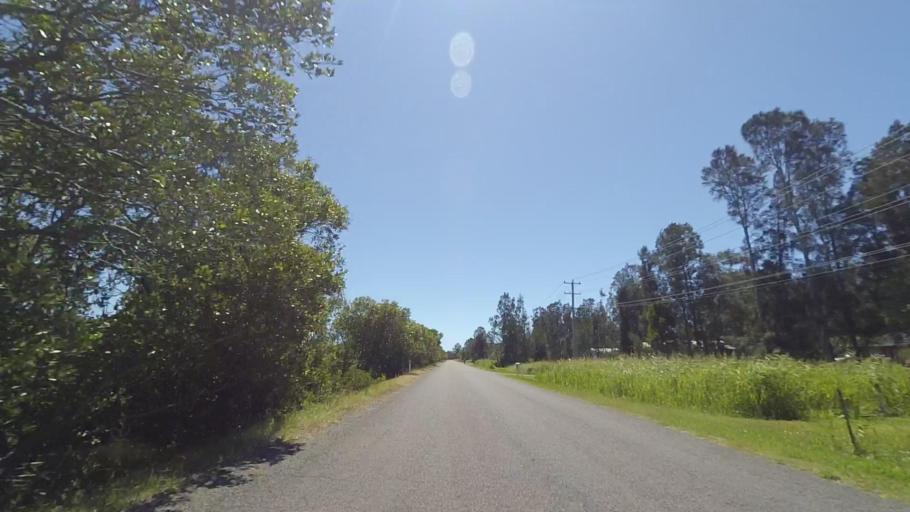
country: AU
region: New South Wales
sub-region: Port Stephens Shire
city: Medowie
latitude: -32.7821
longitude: 151.9443
